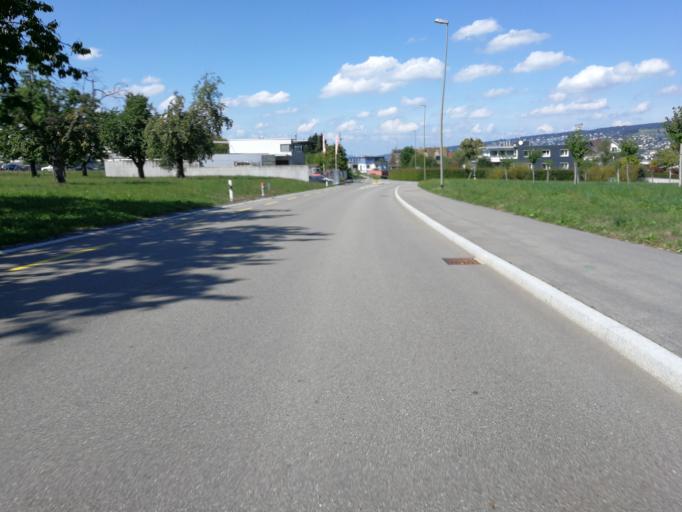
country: CH
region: Zurich
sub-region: Bezirk Horgen
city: Horgen / Allmend
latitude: 47.2498
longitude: 8.6187
